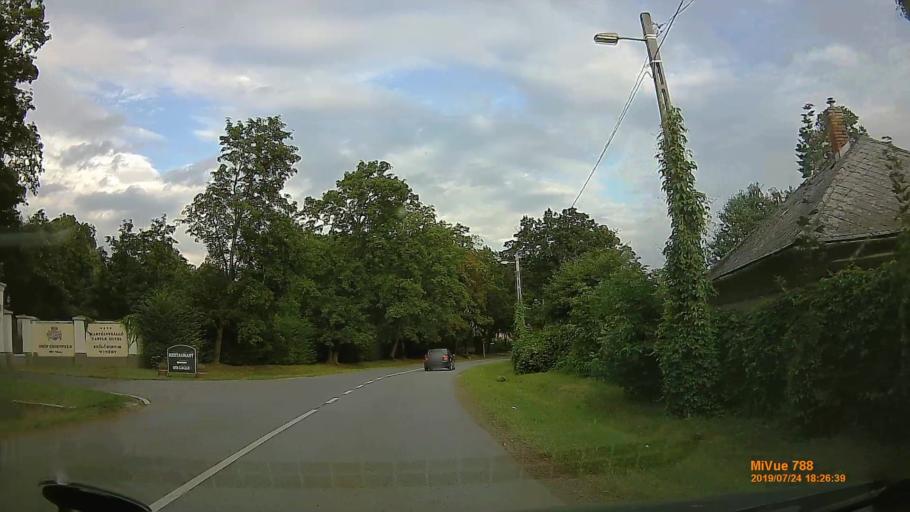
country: HU
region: Borsod-Abauj-Zemplen
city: Tarcal
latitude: 48.1427
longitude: 21.3340
